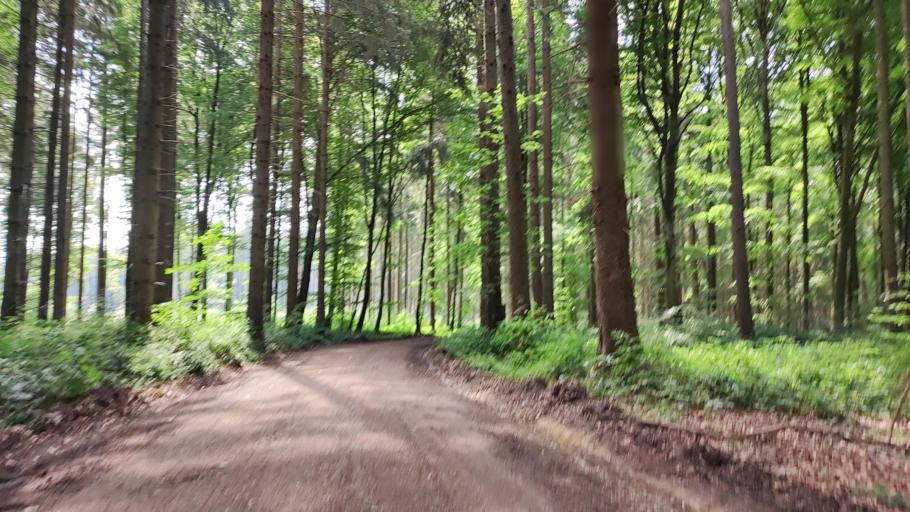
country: DE
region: Bavaria
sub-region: Swabia
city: Adelsried
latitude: 48.4160
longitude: 10.6945
